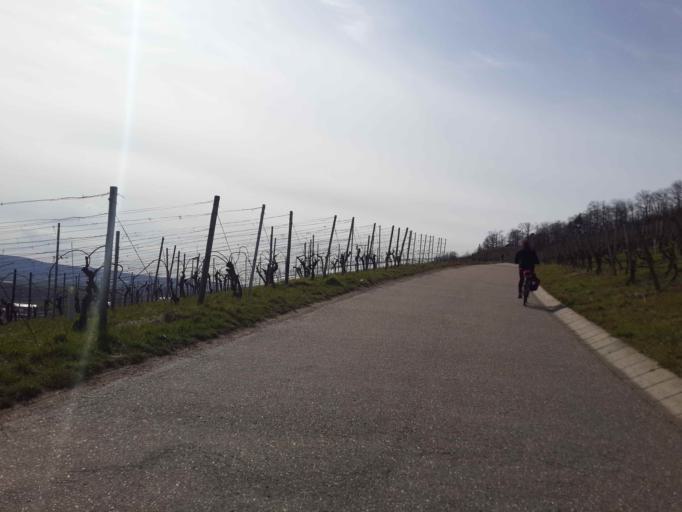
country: DE
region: Baden-Wuerttemberg
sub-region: Regierungsbezirk Stuttgart
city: Brackenheim
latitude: 49.1009
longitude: 9.0769
